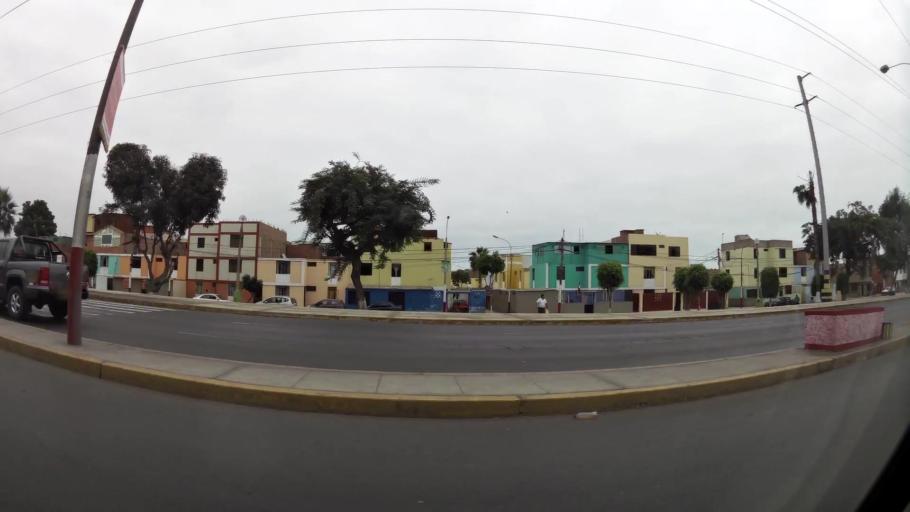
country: PE
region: Callao
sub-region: Callao
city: Callao
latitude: -12.0511
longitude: -77.1283
